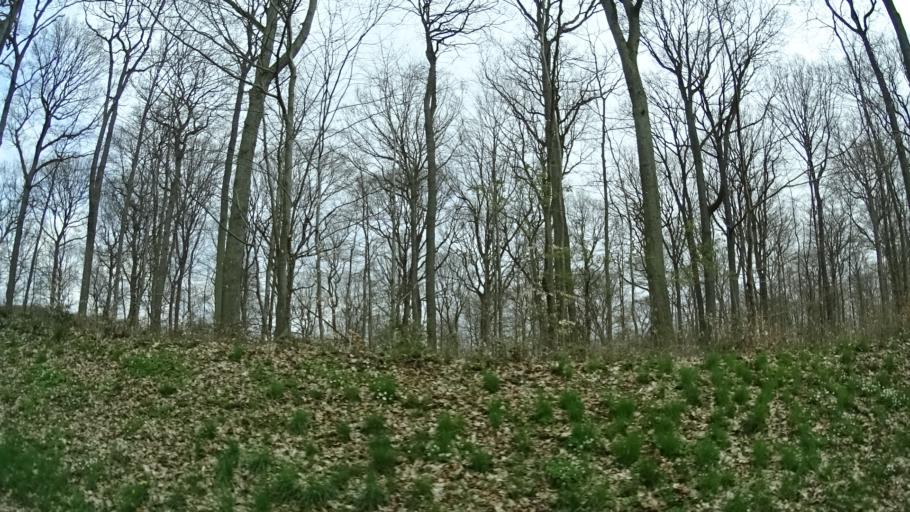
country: DE
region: Rheinland-Pfalz
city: Heinzenberg
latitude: 49.8042
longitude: 7.4756
